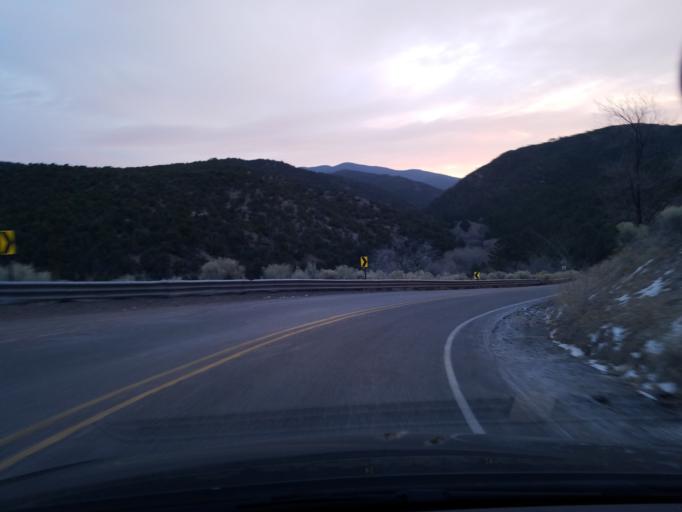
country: US
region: New Mexico
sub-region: Santa Fe County
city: Santa Fe
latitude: 35.7259
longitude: -105.8915
